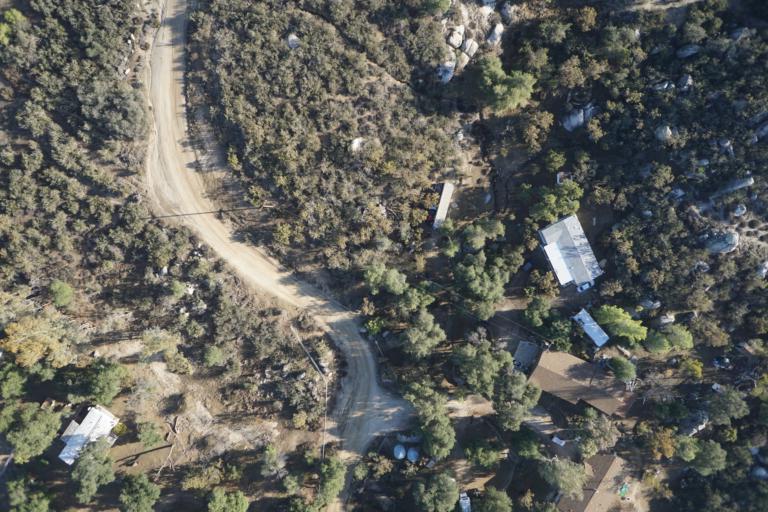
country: US
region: California
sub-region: Riverside County
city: Valle Vista
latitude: 33.6204
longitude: -116.8947
